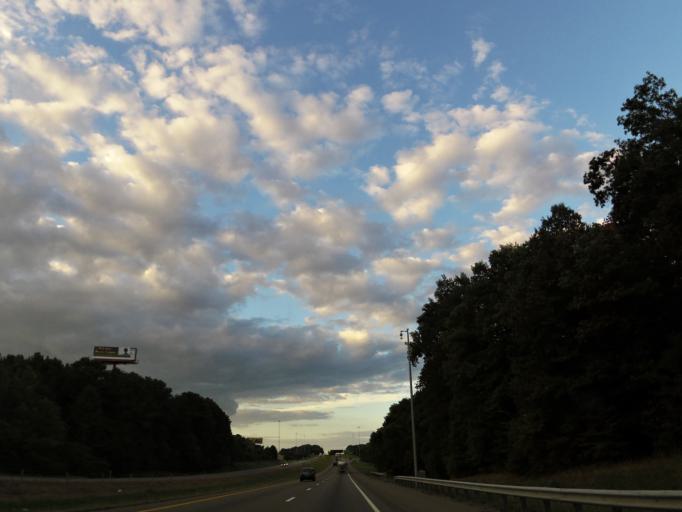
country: US
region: Tennessee
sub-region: Bradley County
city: Hopewell
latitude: 35.2063
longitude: -84.8711
